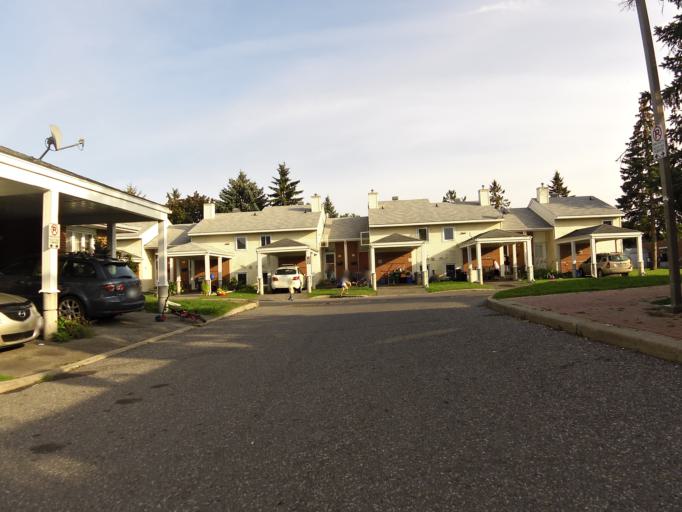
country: CA
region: Ontario
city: Bells Corners
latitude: 45.3464
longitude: -75.7704
